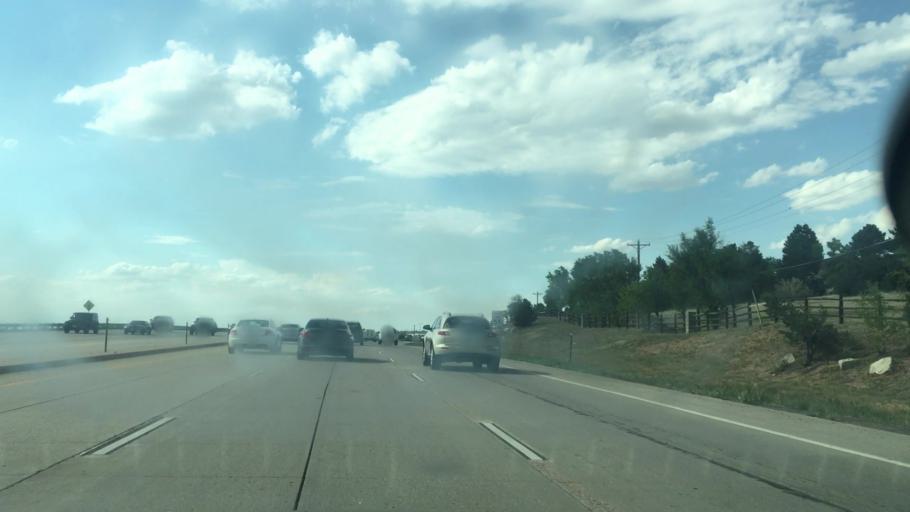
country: US
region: Colorado
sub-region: Arapahoe County
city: Dove Valley
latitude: 39.5740
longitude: -104.7904
